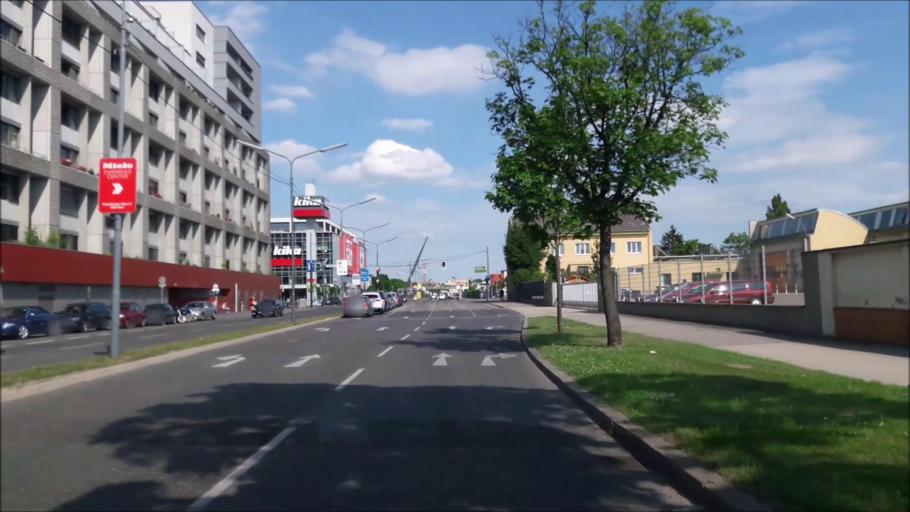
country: AT
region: Vienna
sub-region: Wien Stadt
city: Vienna
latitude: 48.1652
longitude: 16.3668
